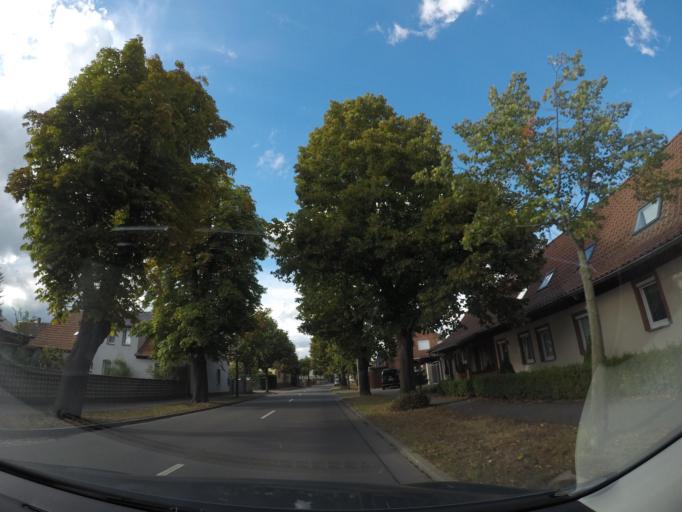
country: DE
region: Saxony-Anhalt
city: Bulstringen
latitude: 52.3186
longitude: 11.3486
